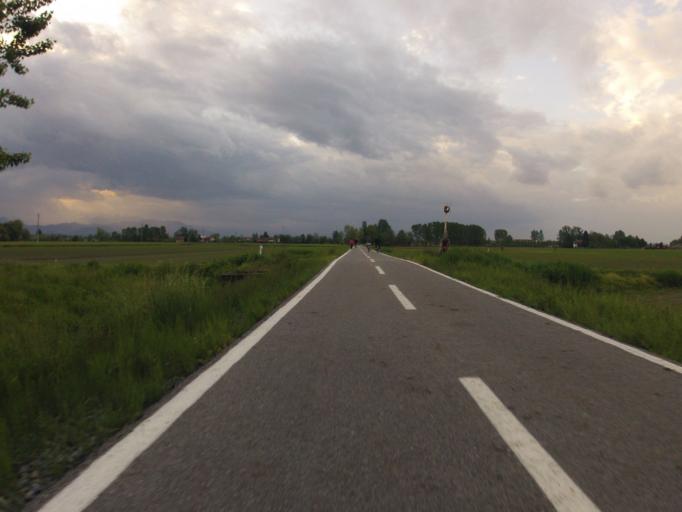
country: IT
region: Piedmont
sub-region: Provincia di Torino
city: Vigone
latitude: 44.8280
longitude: 7.4941
